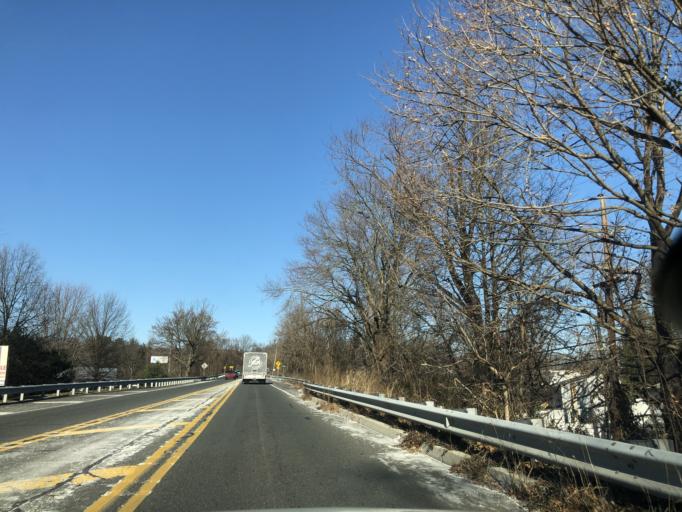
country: US
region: Pennsylvania
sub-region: Bucks County
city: Langhorne Manor
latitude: 40.1627
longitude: -74.8973
